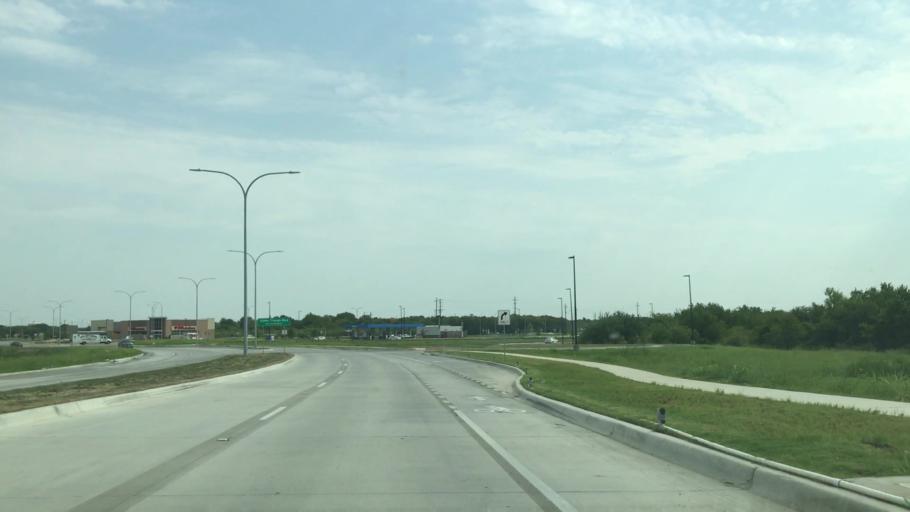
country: US
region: Texas
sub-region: Tarrant County
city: Keller
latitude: 32.9288
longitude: -97.2722
